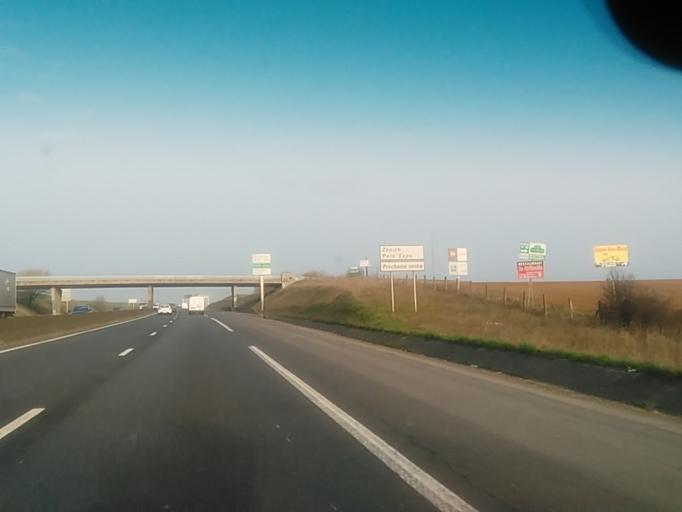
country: FR
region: Lower Normandy
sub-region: Departement du Calvados
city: Louvigny
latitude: 49.1432
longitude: -0.4034
